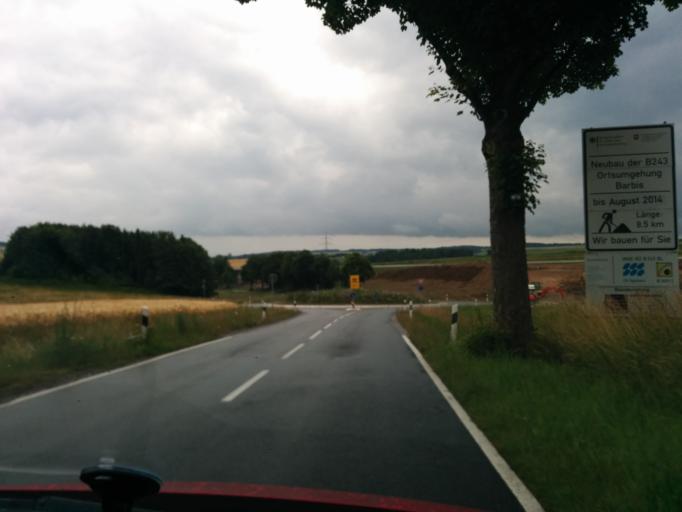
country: DE
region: Lower Saxony
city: Bad Lauterberg im Harz
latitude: 51.6120
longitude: 10.4667
